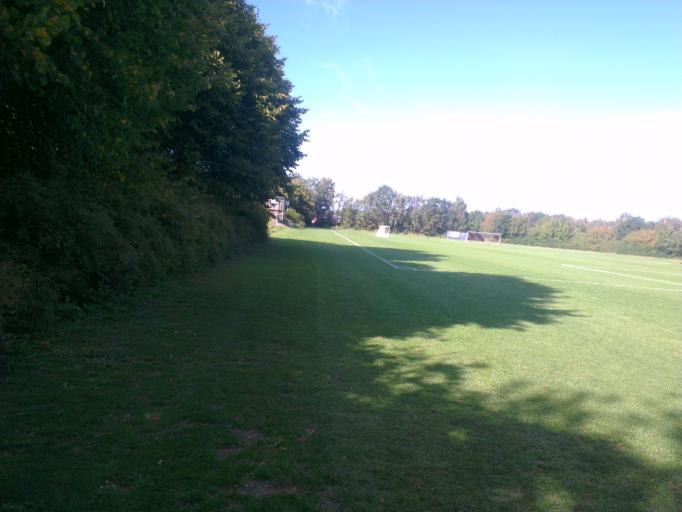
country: DK
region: Capital Region
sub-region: Frederikssund Kommune
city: Jaegerspris
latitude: 55.8425
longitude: 11.9870
